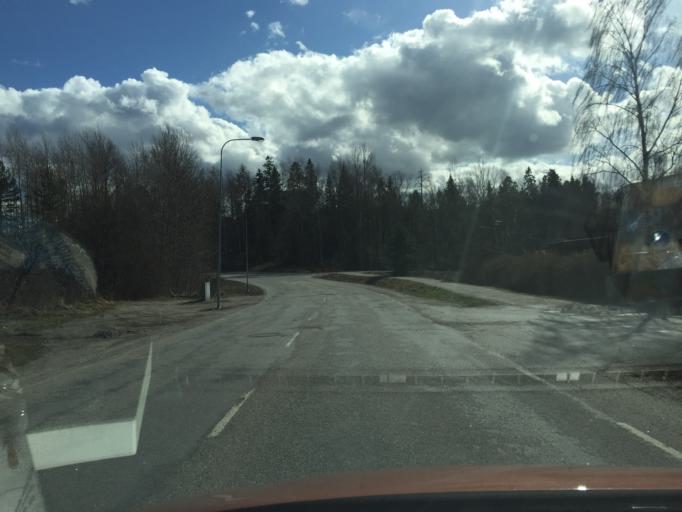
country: SE
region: Stockholm
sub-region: Salems Kommun
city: Ronninge
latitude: 59.2018
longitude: 17.7505
